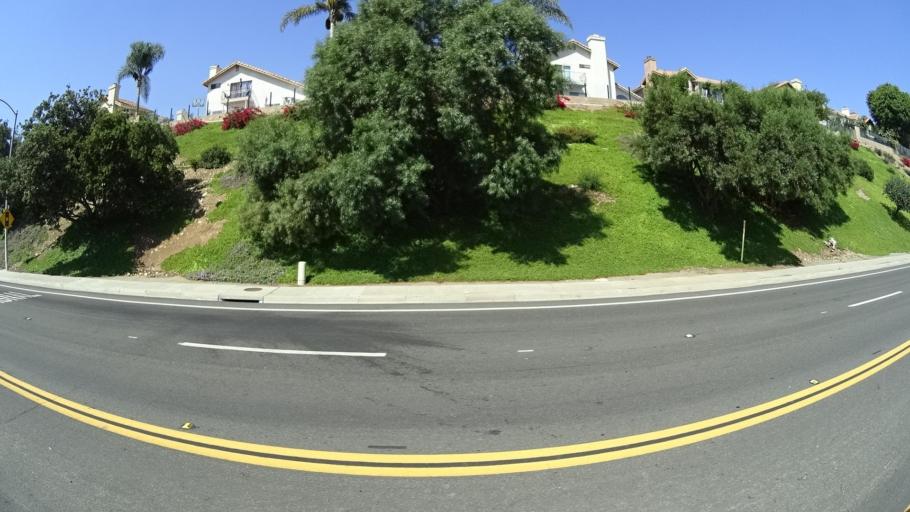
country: US
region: California
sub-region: San Diego County
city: La Presa
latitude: 32.7142
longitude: -116.9790
